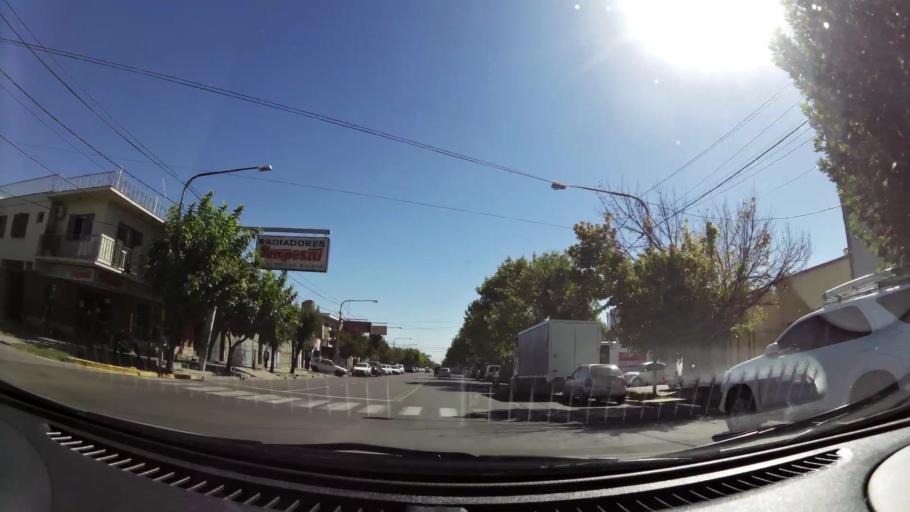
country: AR
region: Mendoza
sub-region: Departamento de Maipu
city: Maipu
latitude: -32.9552
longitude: -68.7887
